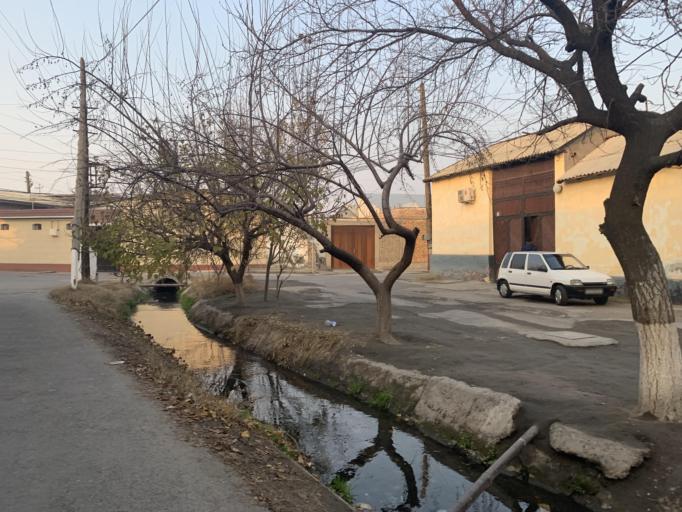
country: UZ
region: Fergana
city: Qo`qon
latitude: 40.5315
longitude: 70.9314
